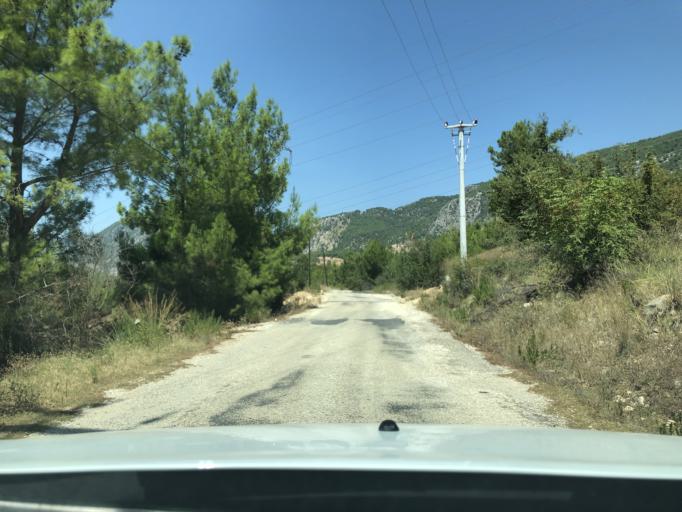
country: TR
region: Antalya
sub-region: Manavgat
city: Manavgat
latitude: 36.8745
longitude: 31.5499
